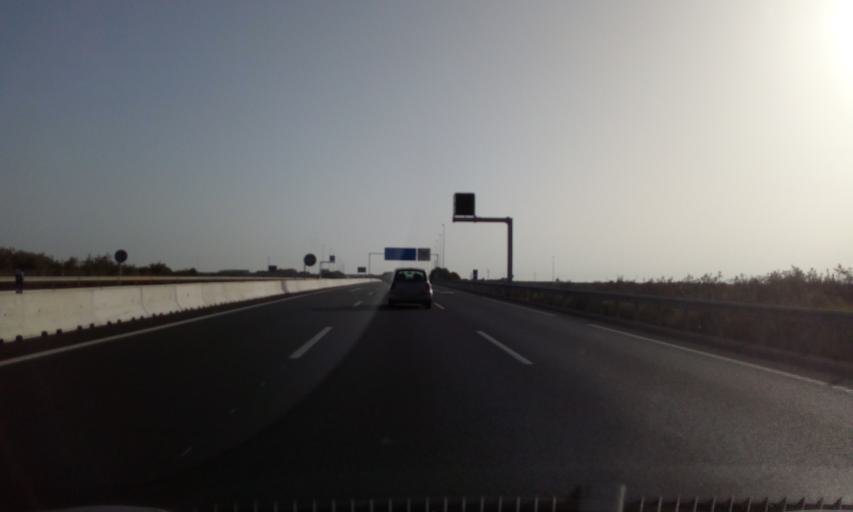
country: ES
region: Andalusia
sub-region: Provincia de Sevilla
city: Benacazon
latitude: 37.3576
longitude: -6.1797
